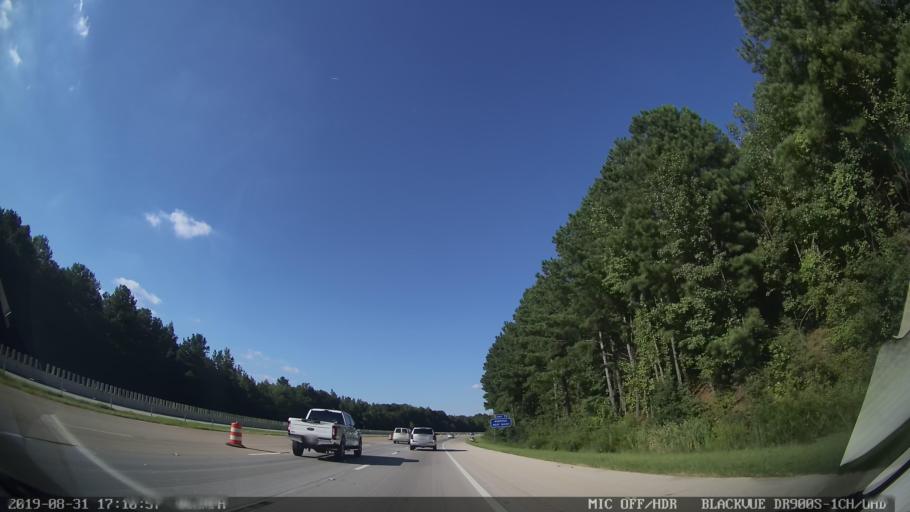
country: US
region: South Carolina
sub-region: Spartanburg County
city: Southern Shops
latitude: 34.9869
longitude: -82.0009
